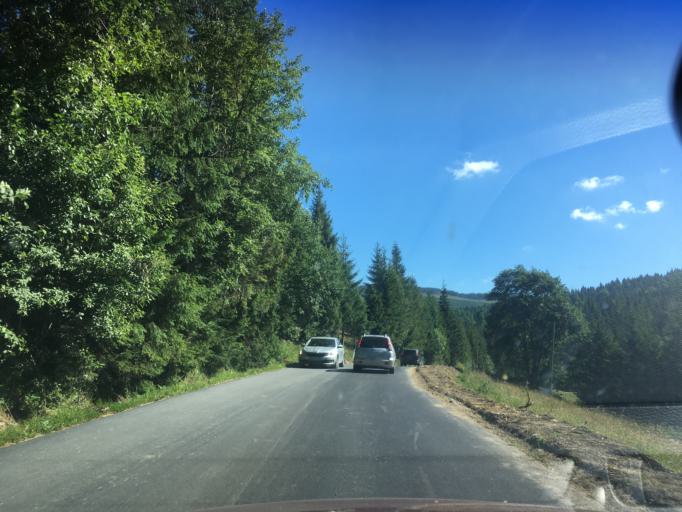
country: SK
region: Presovsky
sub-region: Okres Poprad
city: Zdiar
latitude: 49.2659
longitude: 20.3019
